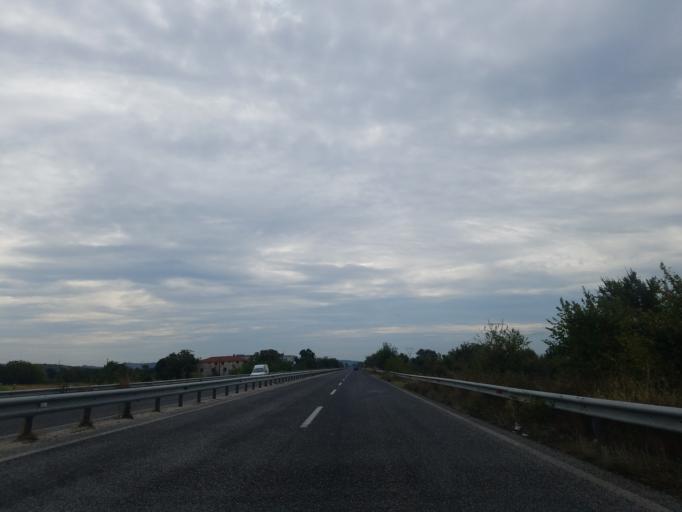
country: GR
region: Thessaly
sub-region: Trikala
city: Vasiliki
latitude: 39.6149
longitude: 21.7174
